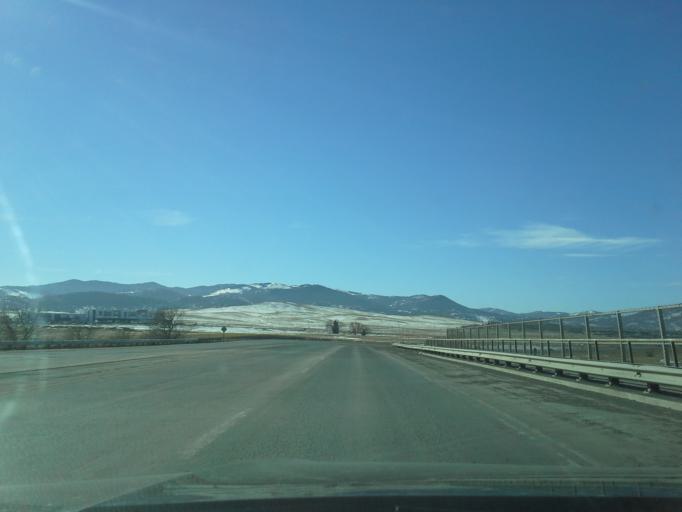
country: US
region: Montana
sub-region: Lewis and Clark County
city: East Helena
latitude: 46.5913
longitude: -111.9471
